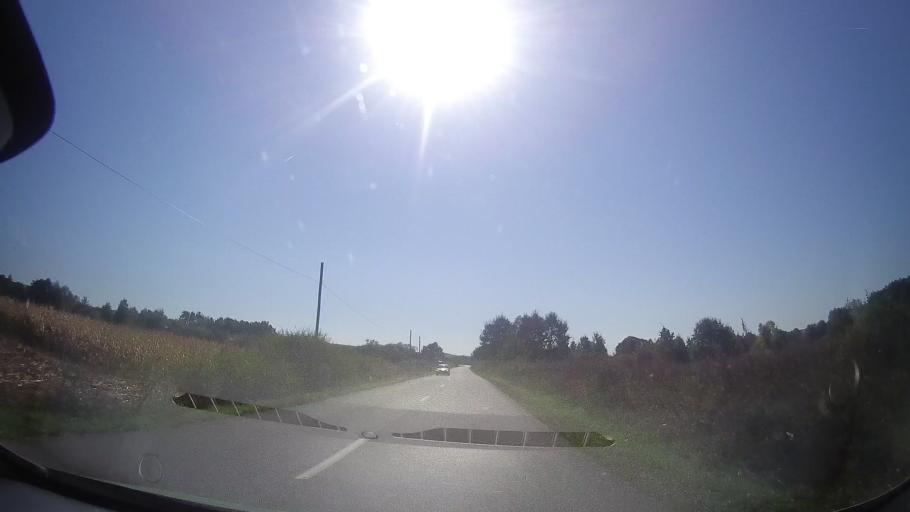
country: RO
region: Timis
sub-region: Comuna Ohaba Lunga
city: Ohaba Lunga
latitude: 45.8728
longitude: 21.9650
